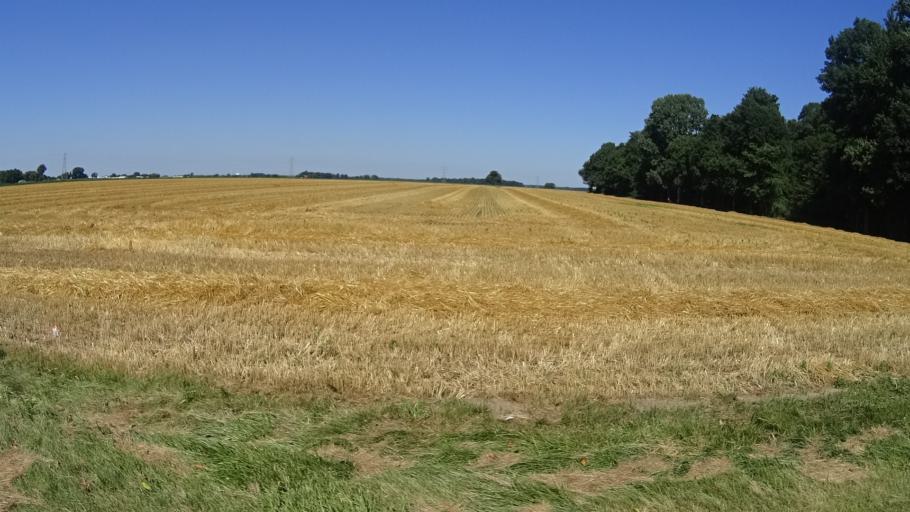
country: US
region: Ohio
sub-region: Erie County
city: Huron
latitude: 41.3698
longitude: -82.5900
